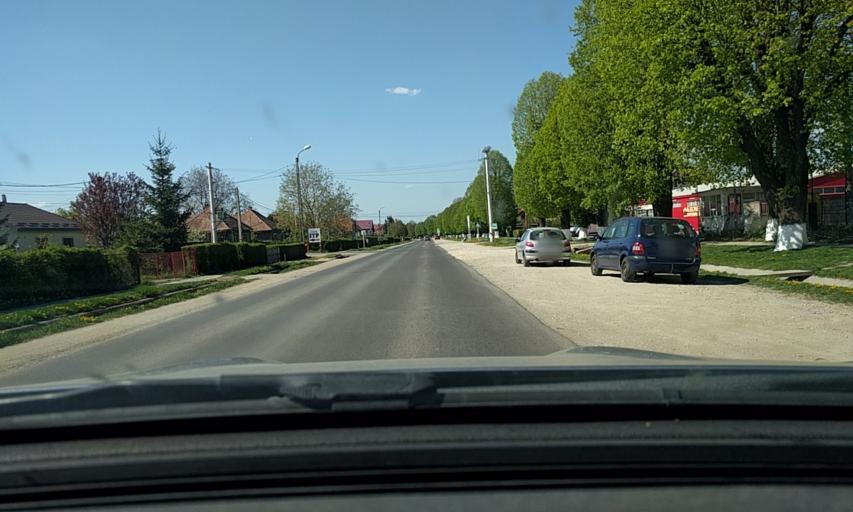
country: RO
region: Brasov
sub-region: Comuna Harman
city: Harman
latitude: 45.7044
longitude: 25.6884
